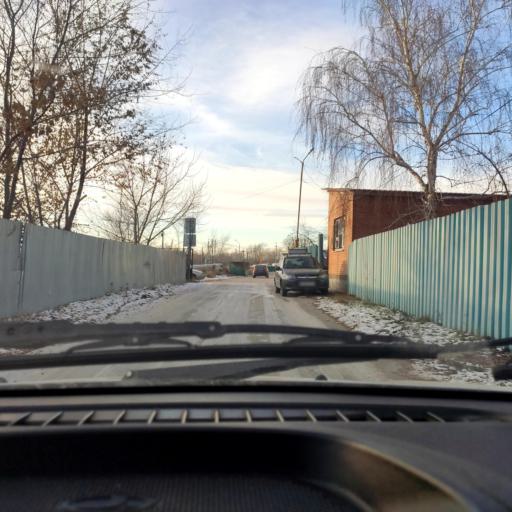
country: RU
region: Samara
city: Zhigulevsk
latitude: 53.4627
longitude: 49.5804
